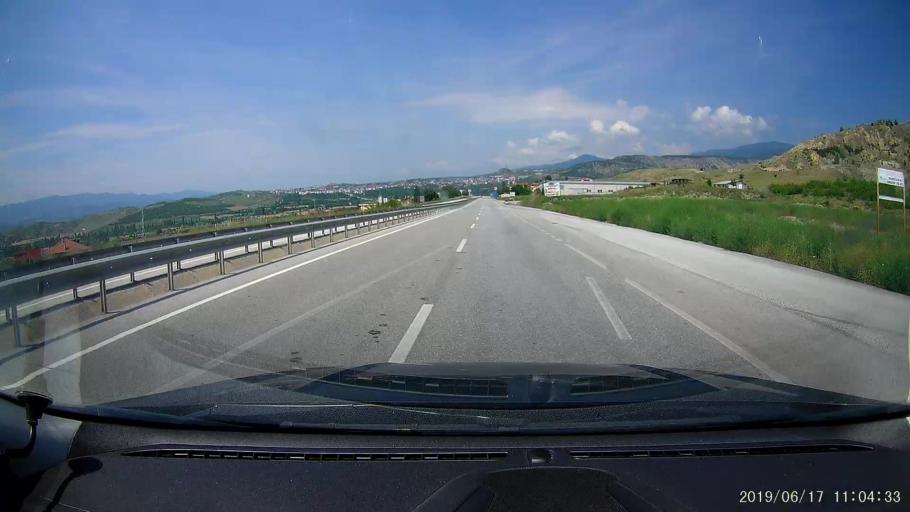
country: TR
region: Kastamonu
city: Tosya
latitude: 41.0199
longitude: 34.0927
